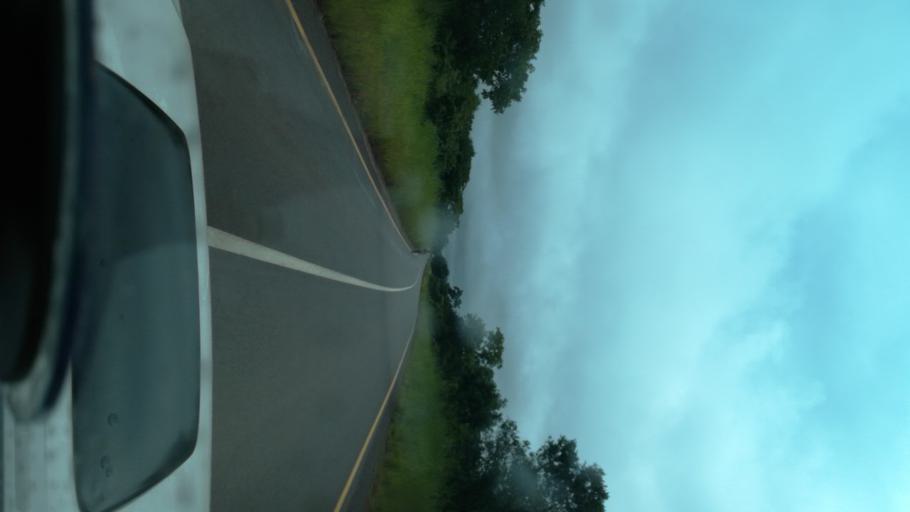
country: CD
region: Katanga
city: Lubumbashi
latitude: -11.0700
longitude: 28.0159
